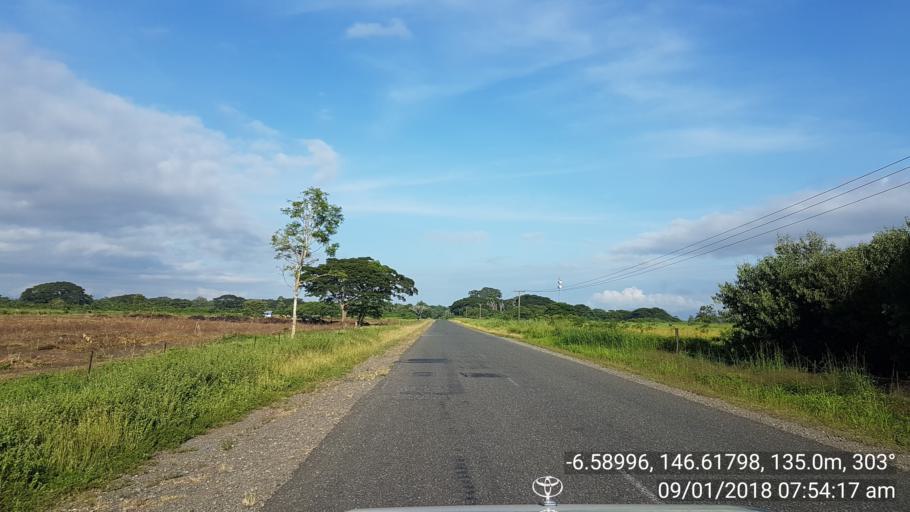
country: PG
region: Morobe
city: Lae
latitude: -6.5900
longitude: 146.6181
